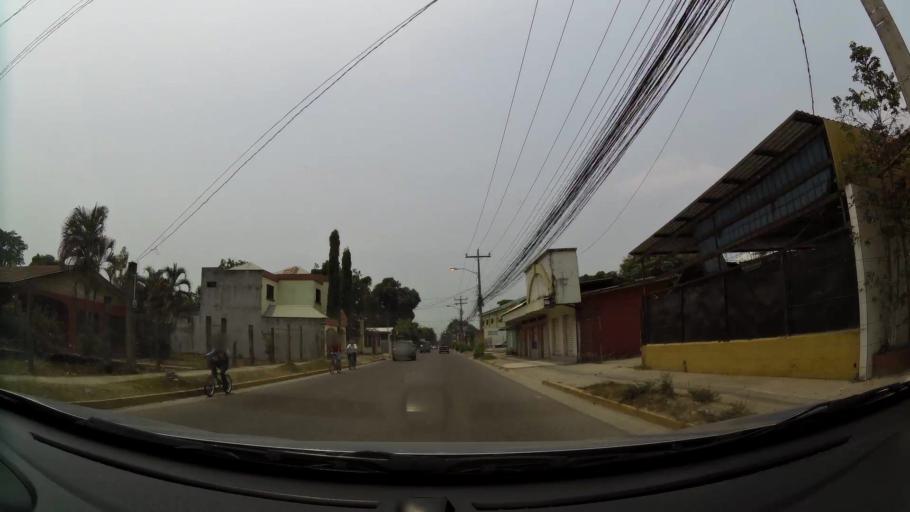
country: HN
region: Yoro
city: El Progreso
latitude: 15.3961
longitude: -87.8085
